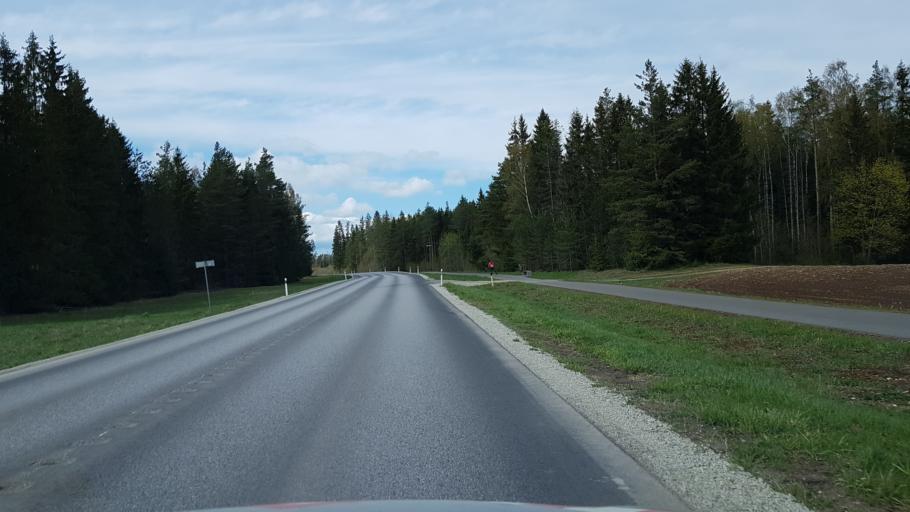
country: EE
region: Laeaene-Virumaa
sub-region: Vinni vald
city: Vinni
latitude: 59.2605
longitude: 26.4553
